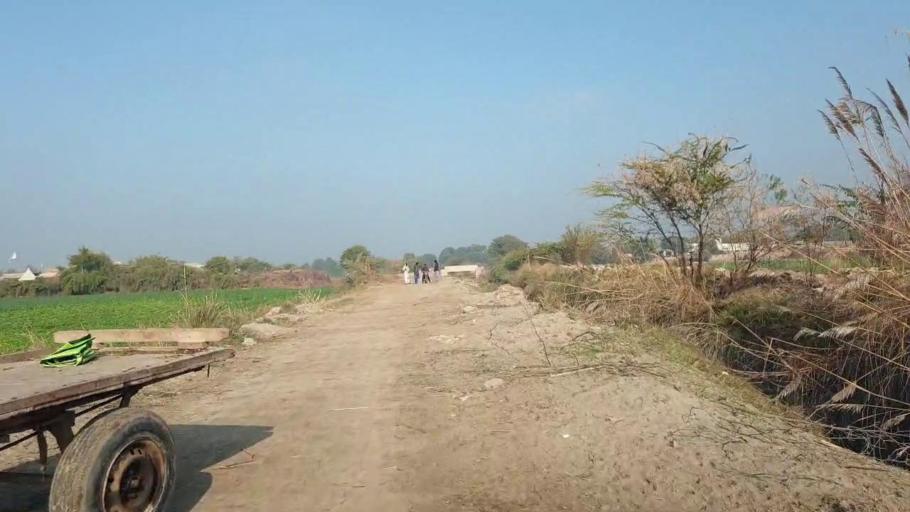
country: PK
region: Sindh
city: Shahdadpur
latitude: 25.9711
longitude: 68.6138
